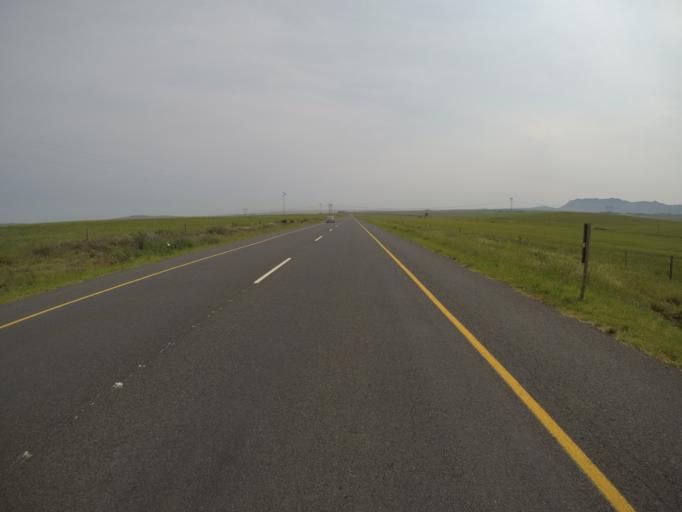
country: ZA
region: Western Cape
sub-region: West Coast District Municipality
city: Malmesbury
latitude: -33.4981
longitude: 18.8316
